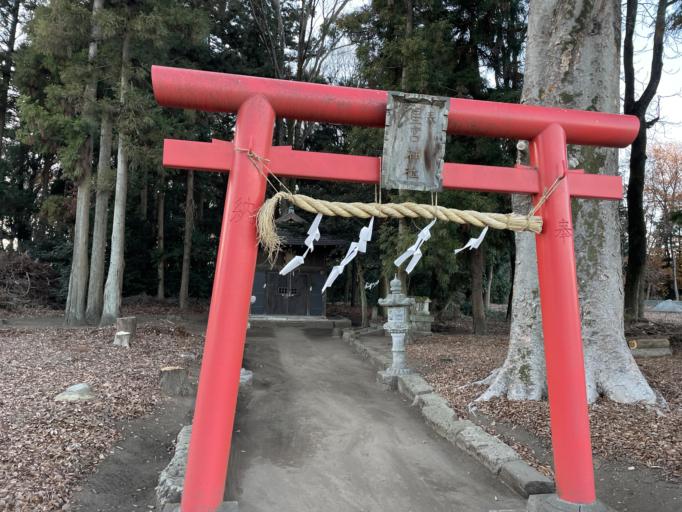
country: JP
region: Tochigi
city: Kaminokawa
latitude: 36.4607
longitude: 139.8690
